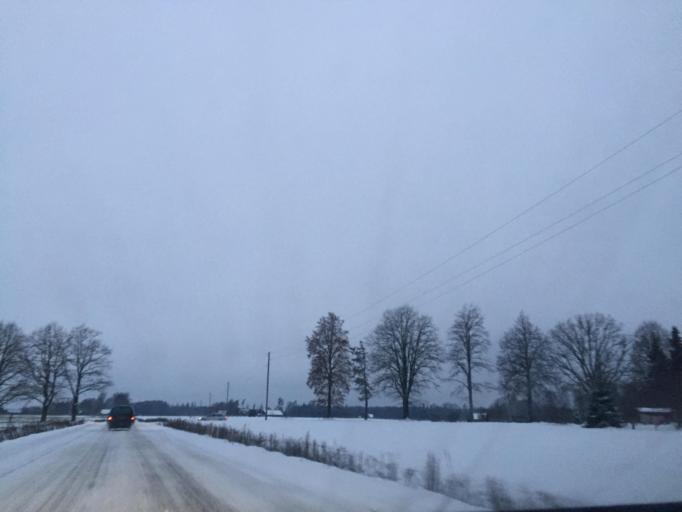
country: LV
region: Raunas
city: Rauna
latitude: 57.4317
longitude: 25.6179
